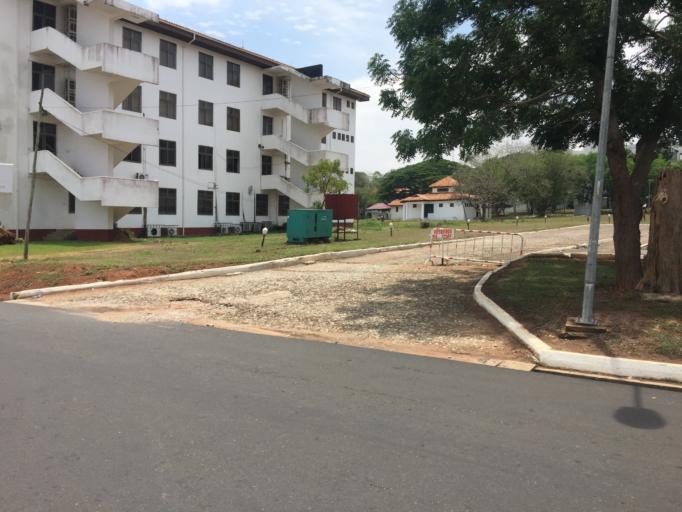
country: GH
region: Greater Accra
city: Medina Estates
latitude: 5.6526
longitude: -0.1878
